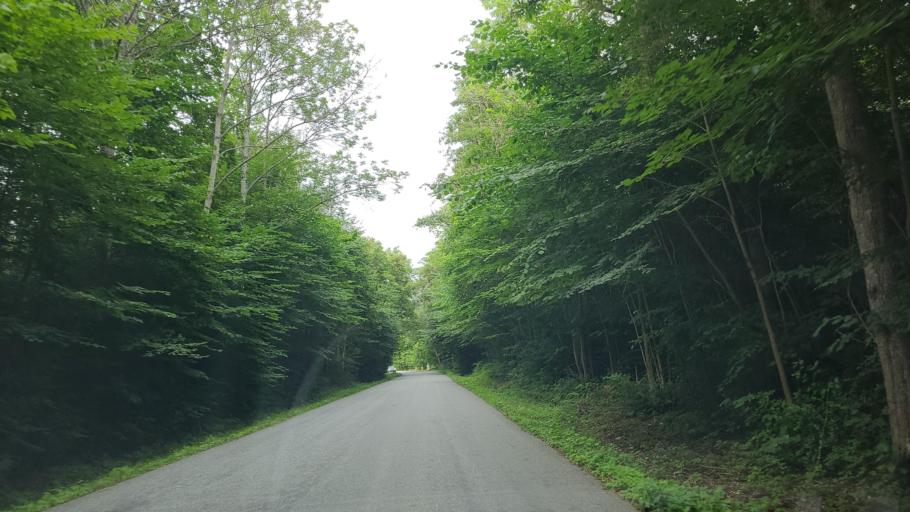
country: SE
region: Stockholm
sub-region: Upplands-Bro Kommun
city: Bro
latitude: 59.4811
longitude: 17.5653
